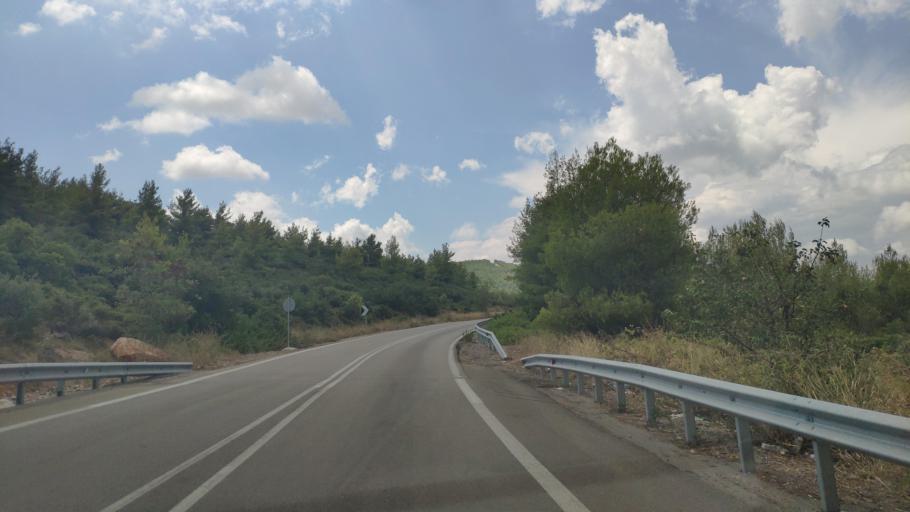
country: GR
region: Central Greece
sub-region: Nomos Fthiotidos
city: Martinon
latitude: 38.6093
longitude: 23.1799
